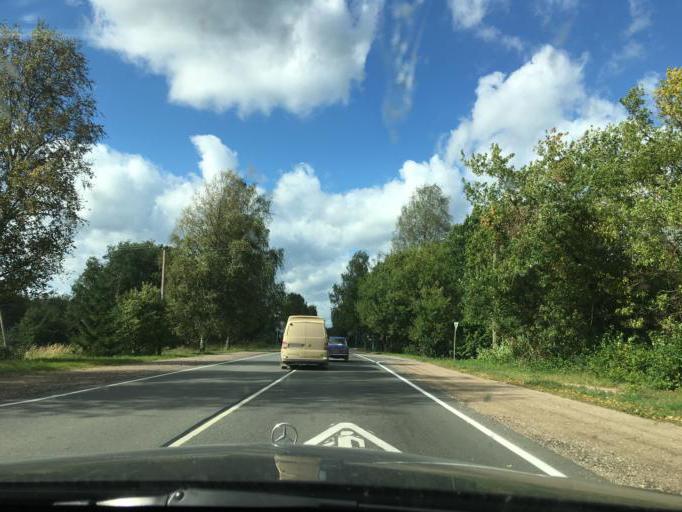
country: RU
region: Pskov
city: Pustoshka
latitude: 56.4013
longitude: 29.2300
